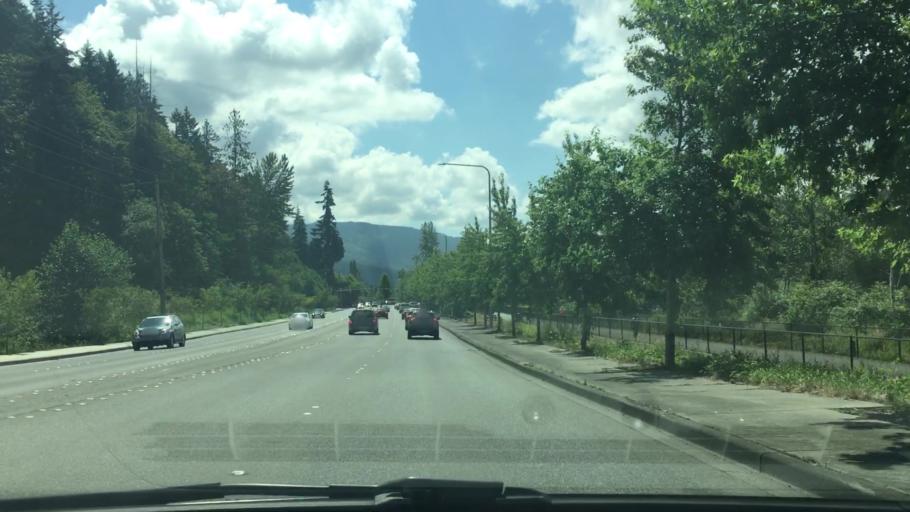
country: US
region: Washington
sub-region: King County
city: Issaquah
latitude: 47.5590
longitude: -122.0480
